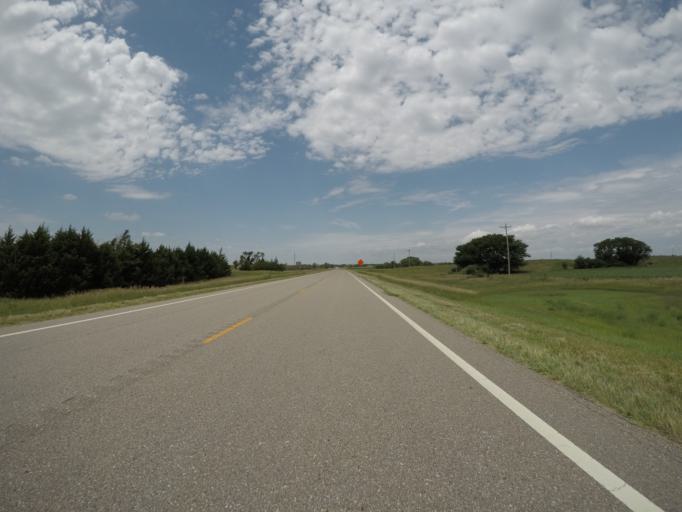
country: US
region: Kansas
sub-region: Graham County
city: Hill City
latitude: 39.3944
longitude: -99.6187
